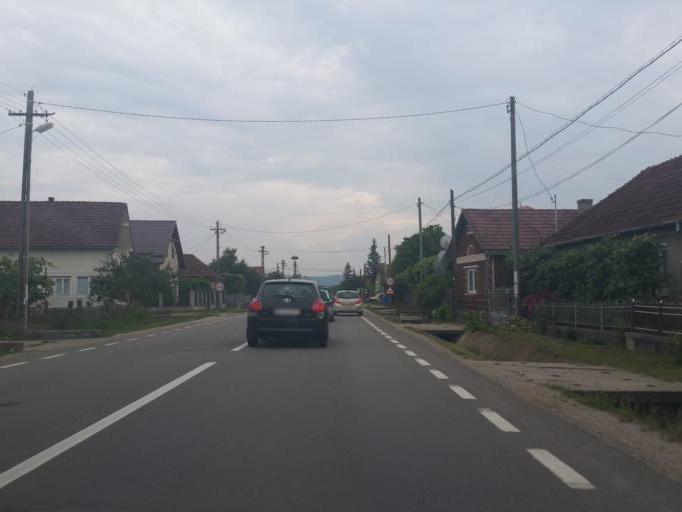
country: RO
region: Salaj
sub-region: Comuna Zimbor
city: Zimbor
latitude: 47.0077
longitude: 23.2606
